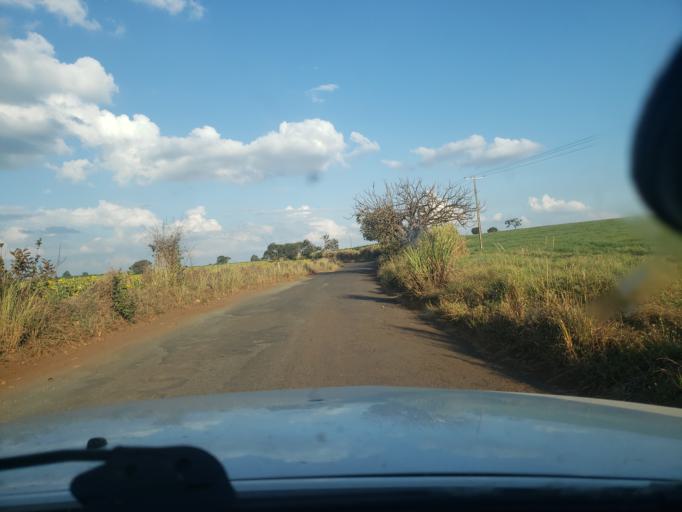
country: BR
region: Sao Paulo
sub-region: Mogi-Mirim
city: Mogi Mirim
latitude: -22.4694
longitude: -46.9298
